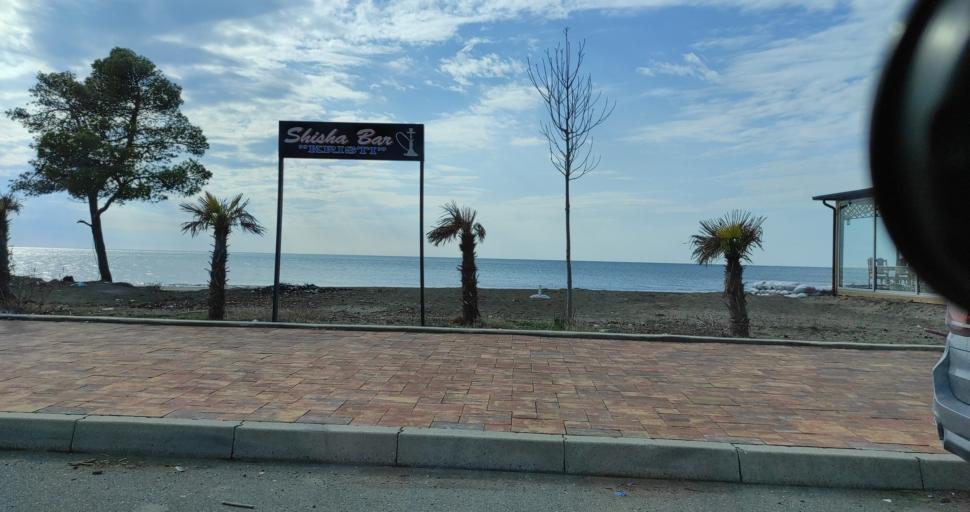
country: AL
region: Lezhe
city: Shengjin
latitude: 41.7992
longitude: 19.6014
